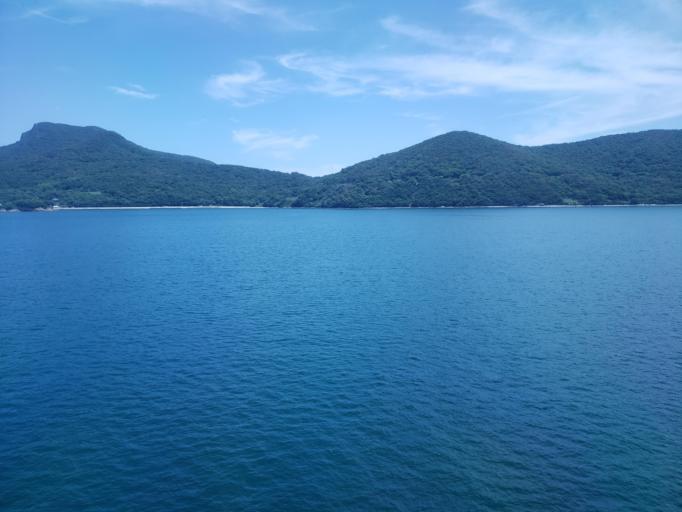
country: JP
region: Kagawa
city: Tonosho
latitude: 34.4375
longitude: 134.3195
